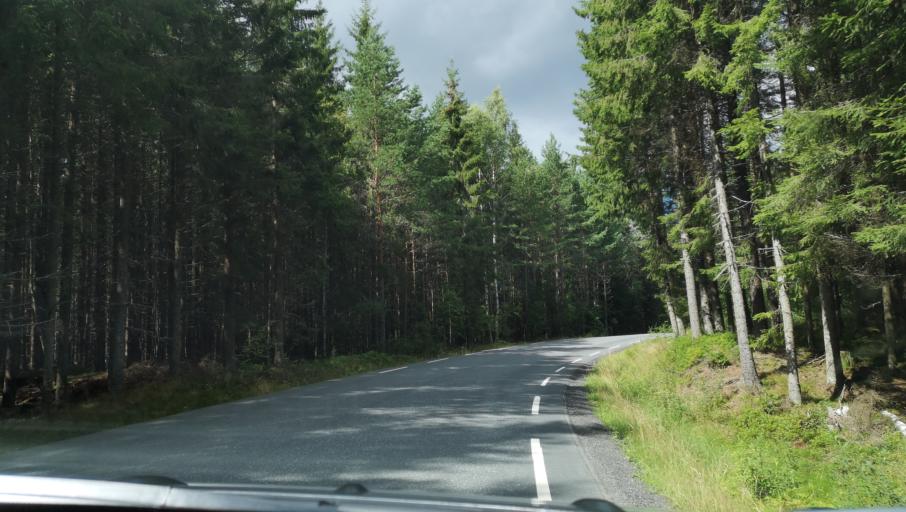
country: NO
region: Ostfold
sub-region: Hobol
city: Tomter
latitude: 59.6774
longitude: 10.9557
